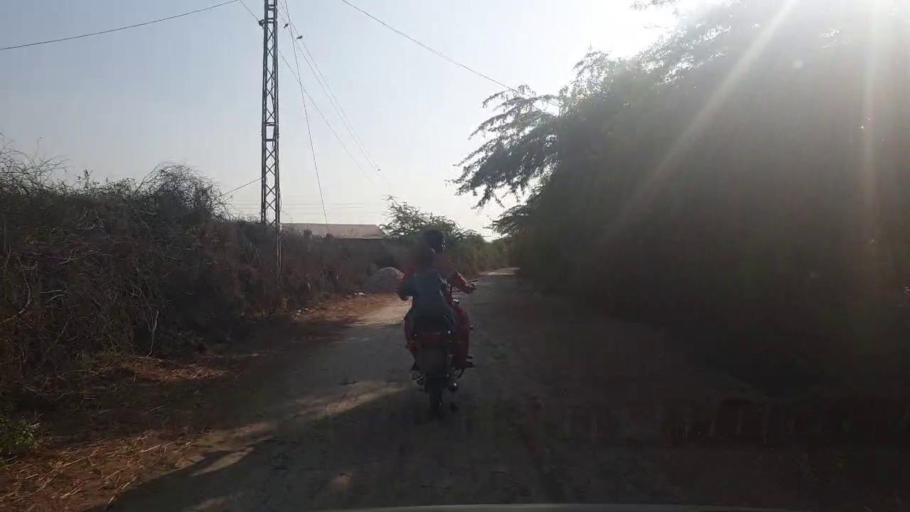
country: PK
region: Sindh
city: Badin
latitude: 24.6453
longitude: 68.8042
